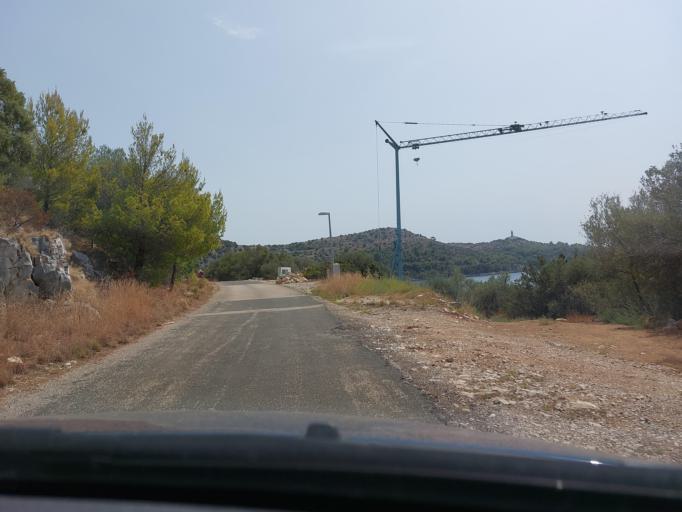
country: HR
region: Dubrovacko-Neretvanska
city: Smokvica
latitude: 42.7359
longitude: 16.8893
